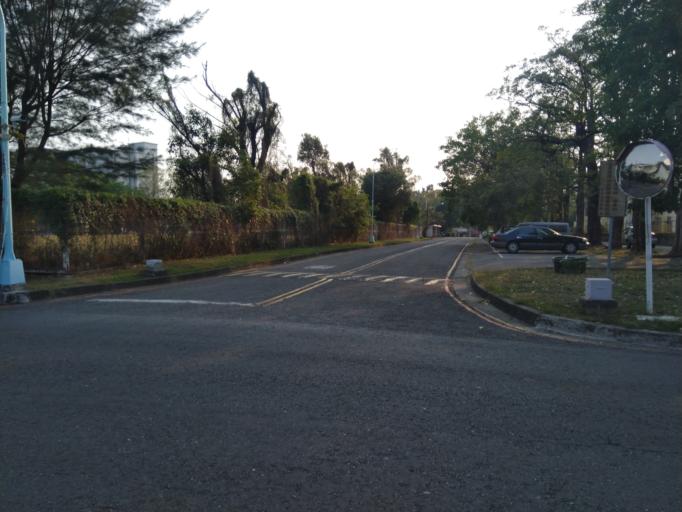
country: TW
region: Kaohsiung
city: Kaohsiung
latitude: 22.7113
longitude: 120.3057
